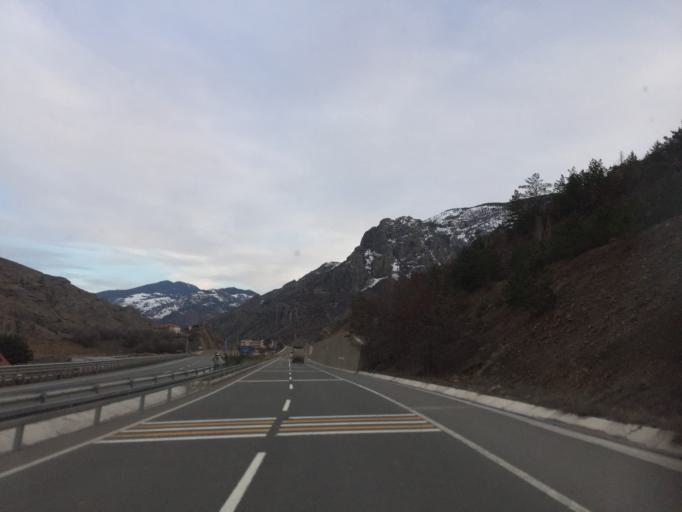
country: TR
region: Gumushane
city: Gumushkhane
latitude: 40.5045
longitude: 39.4247
